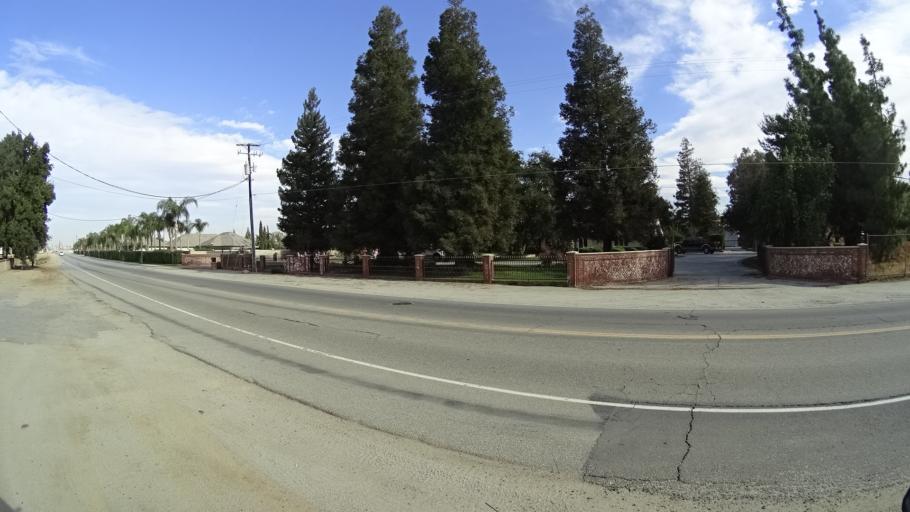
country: US
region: California
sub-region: Kern County
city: Greenacres
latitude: 35.4228
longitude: -119.0923
